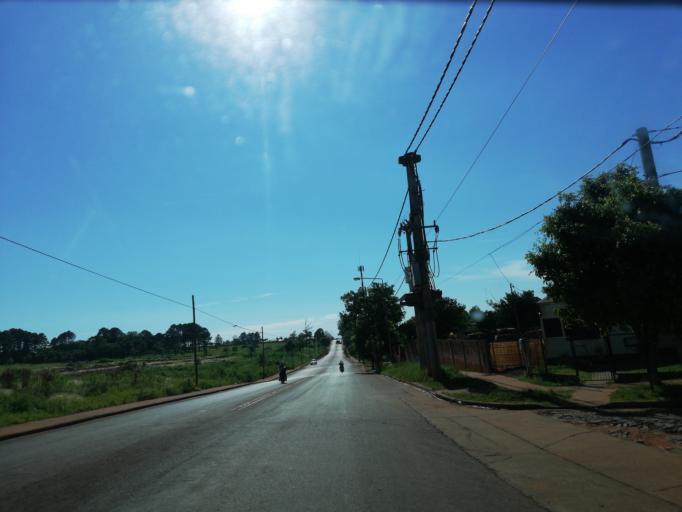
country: AR
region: Misiones
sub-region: Departamento de Capital
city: Posadas
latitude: -27.4335
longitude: -55.9362
